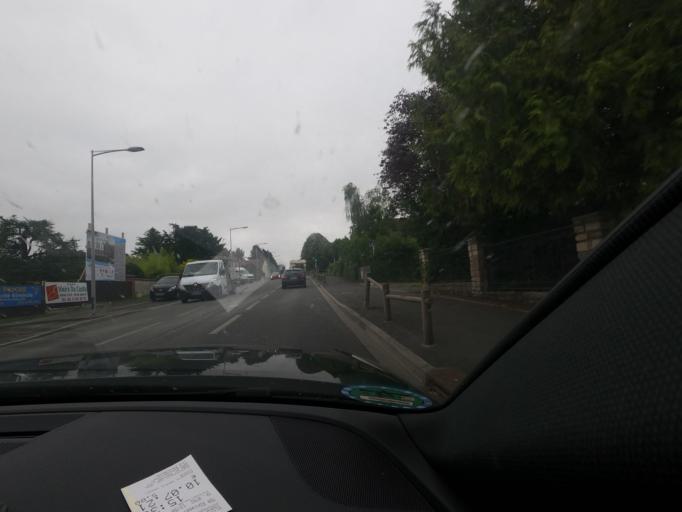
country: FR
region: Picardie
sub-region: Departement de la Somme
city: Amiens
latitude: 49.8669
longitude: 2.3082
